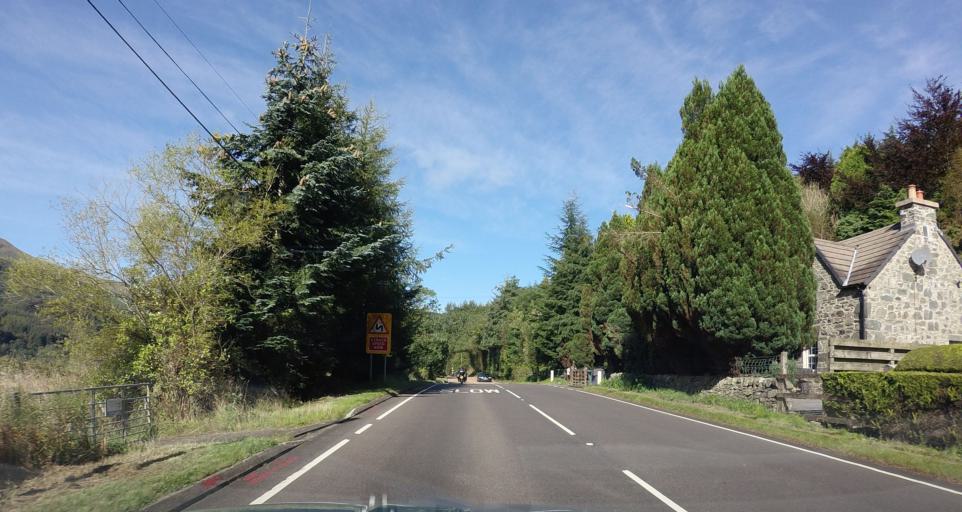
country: GB
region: Scotland
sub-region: Stirling
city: Callander
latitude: 56.3013
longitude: -4.3116
